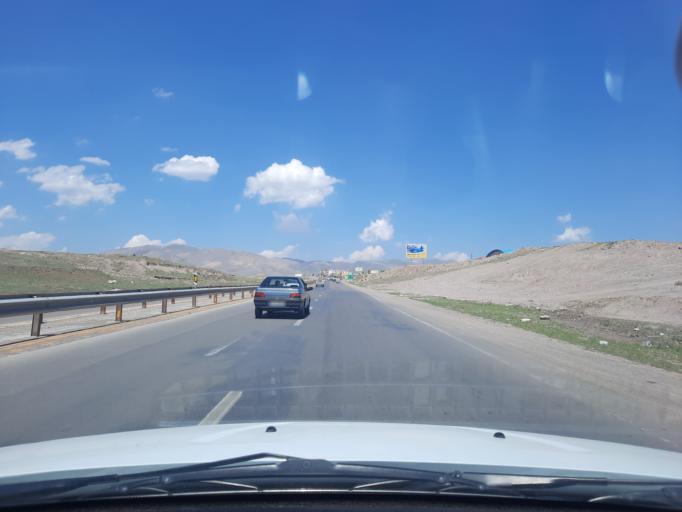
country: IR
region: Qazvin
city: Alvand
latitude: 36.2821
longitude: 50.1293
